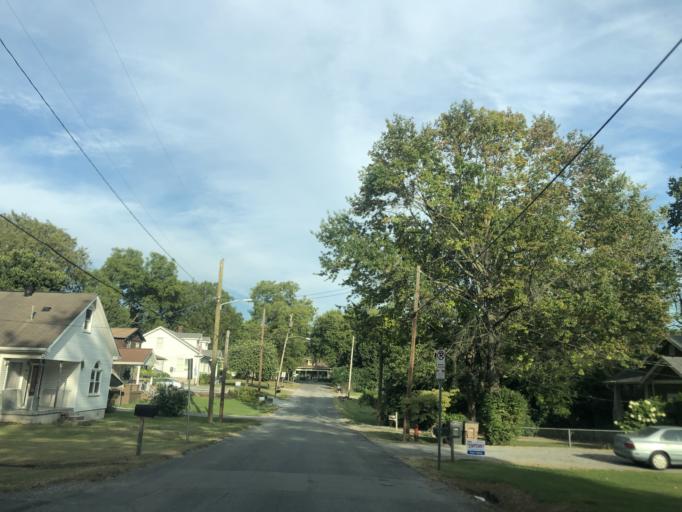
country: US
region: Tennessee
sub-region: Davidson County
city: Oak Hill
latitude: 36.1187
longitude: -86.7449
